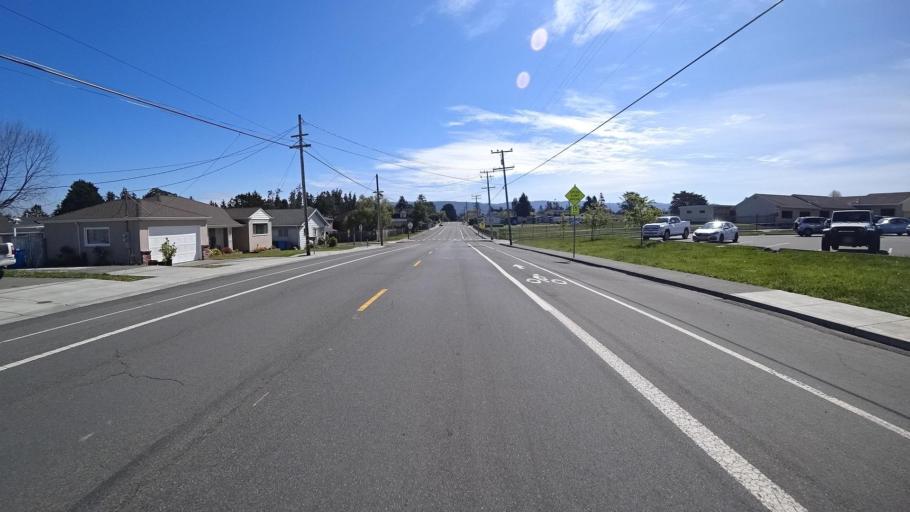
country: US
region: California
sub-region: Humboldt County
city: Myrtletown
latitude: 40.7951
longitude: -124.1324
